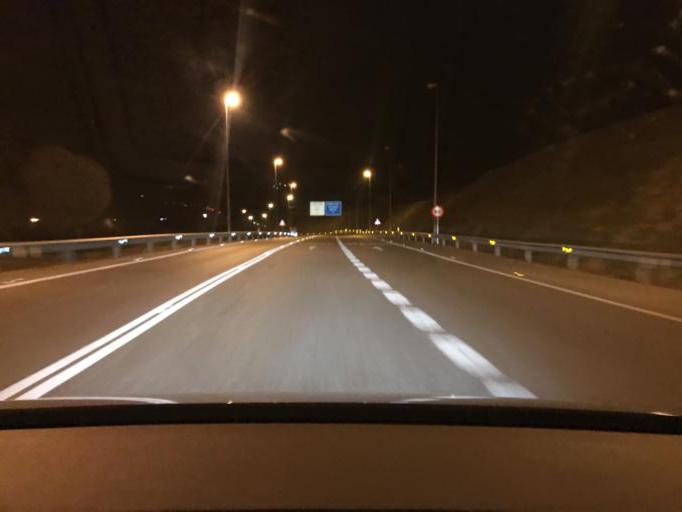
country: ES
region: Andalusia
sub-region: Provincia de Jaen
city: Jaen
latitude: 37.7804
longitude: -3.7529
